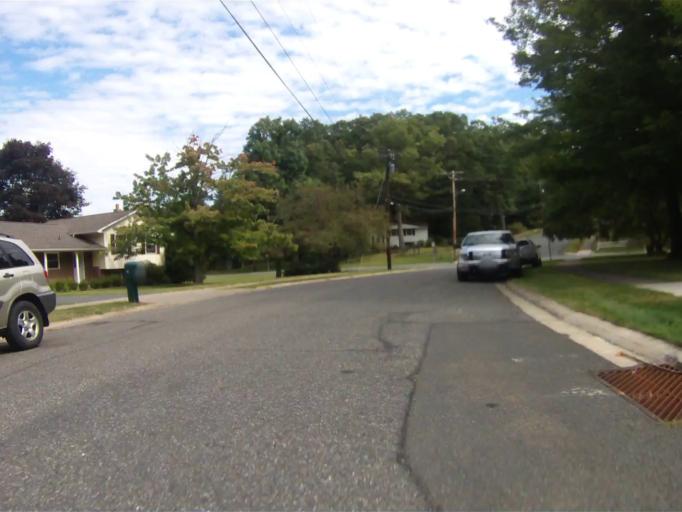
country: US
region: Pennsylvania
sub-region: Centre County
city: Park Forest Village
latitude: 40.8093
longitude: -77.9152
